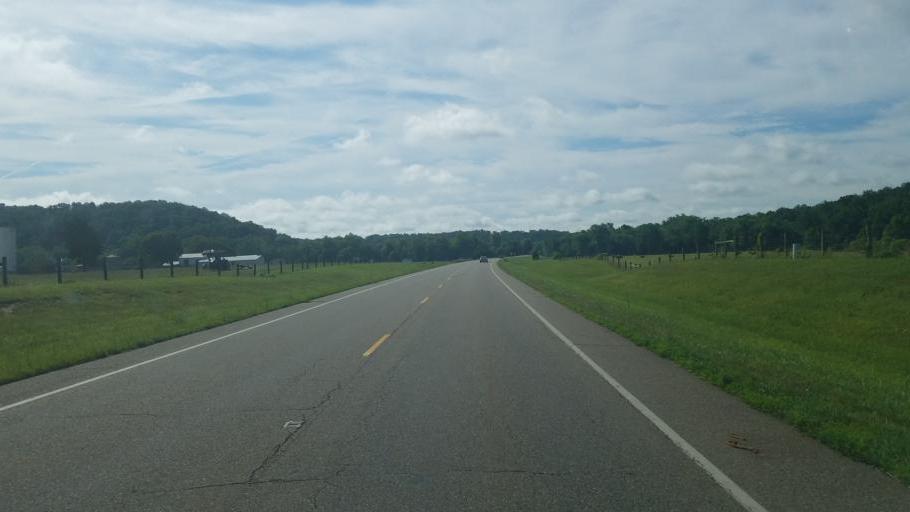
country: US
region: Ohio
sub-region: Gallia County
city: Gallipolis
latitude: 38.8781
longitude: -82.3619
